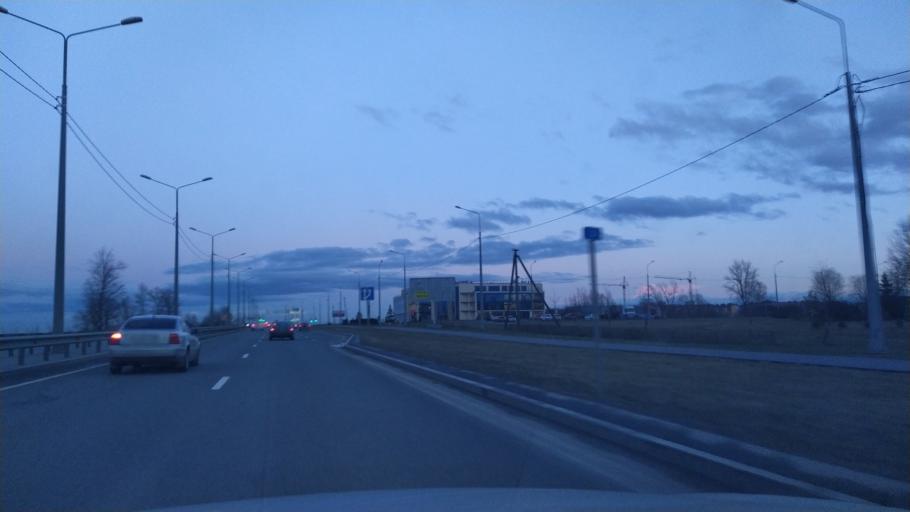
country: RU
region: St.-Petersburg
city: Aleksandrovskaya
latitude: 59.7618
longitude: 30.3651
